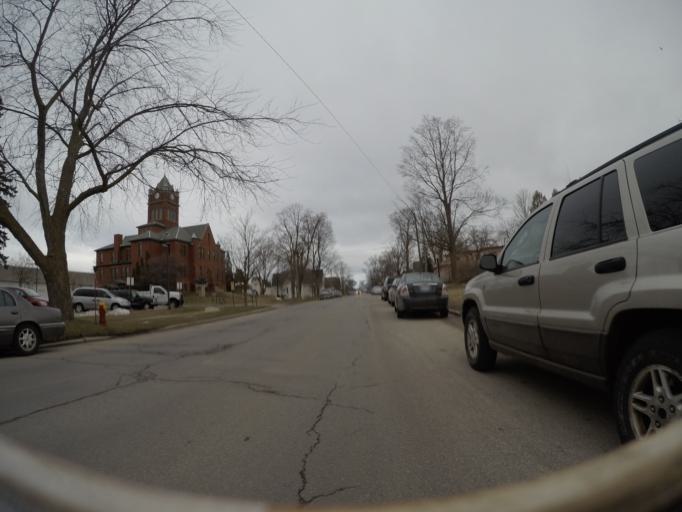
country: US
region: Michigan
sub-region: Grand Traverse County
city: Traverse City
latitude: 44.7608
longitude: -85.6157
